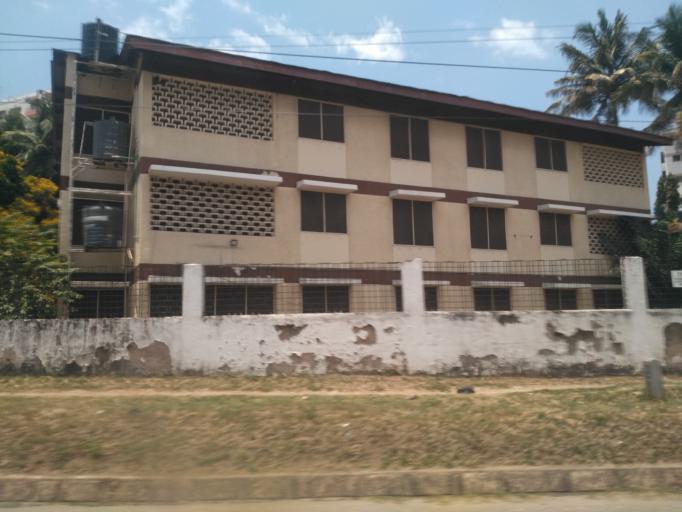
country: TZ
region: Dar es Salaam
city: Dar es Salaam
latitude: -6.8066
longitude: 39.2814
